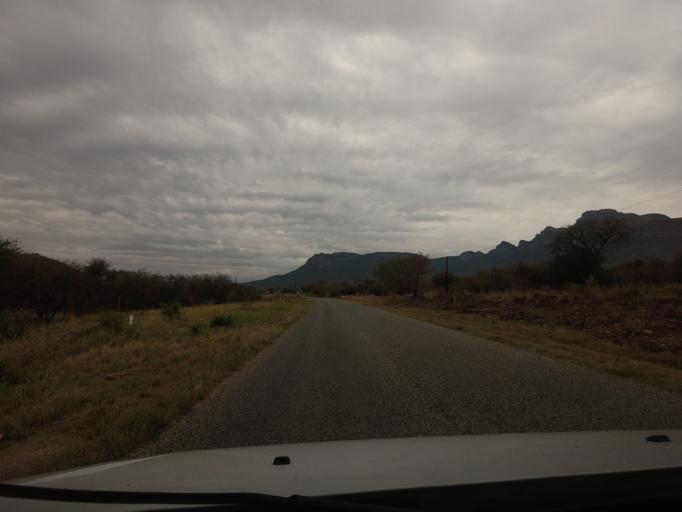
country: ZA
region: Limpopo
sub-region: Mopani District Municipality
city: Hoedspruit
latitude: -24.4971
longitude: 30.8930
